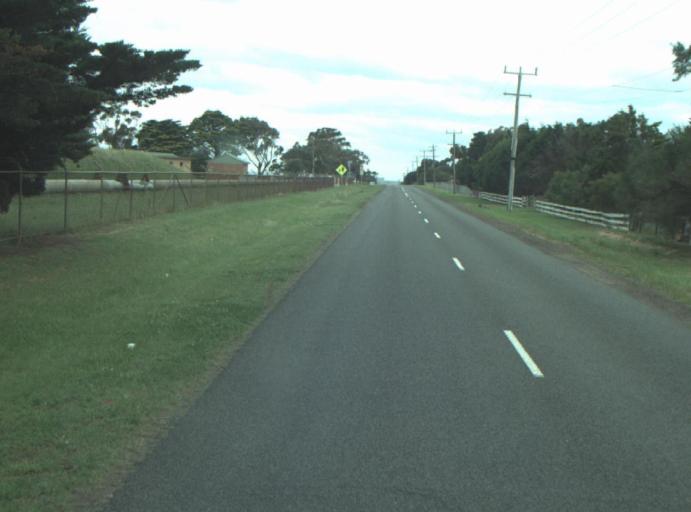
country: AU
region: Victoria
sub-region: Greater Geelong
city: Bell Post Hill
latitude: -38.0647
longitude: 144.3255
